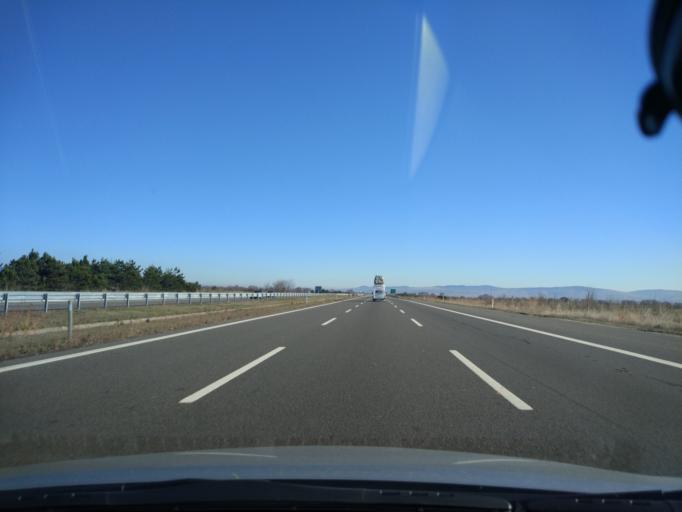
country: TR
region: Bolu
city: Gerede
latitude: 40.7391
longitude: 32.1478
